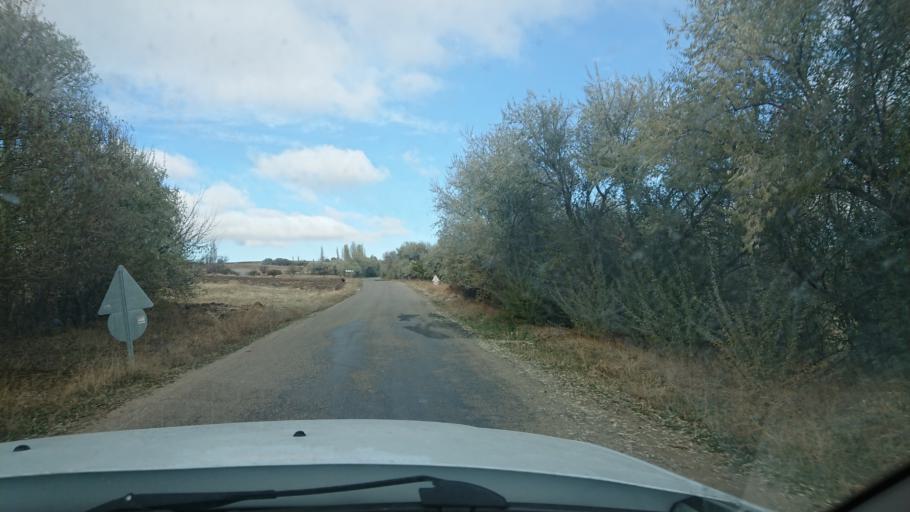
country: TR
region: Aksaray
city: Agacoren
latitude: 38.8286
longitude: 33.9571
